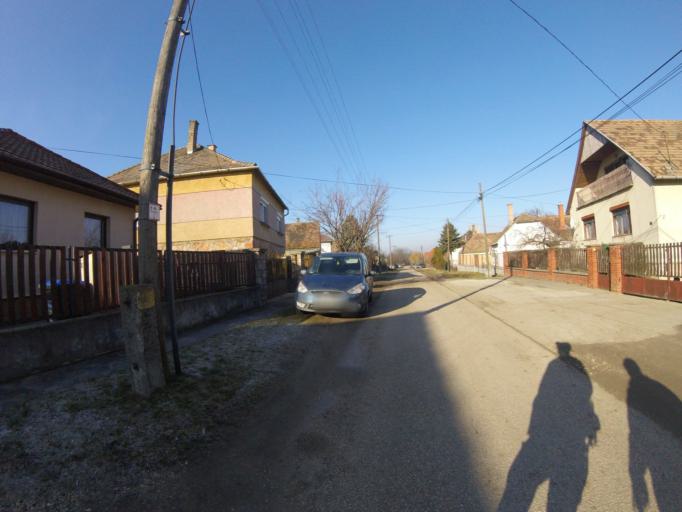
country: HU
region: Komarom-Esztergom
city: Bokod
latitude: 47.5209
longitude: 18.2185
